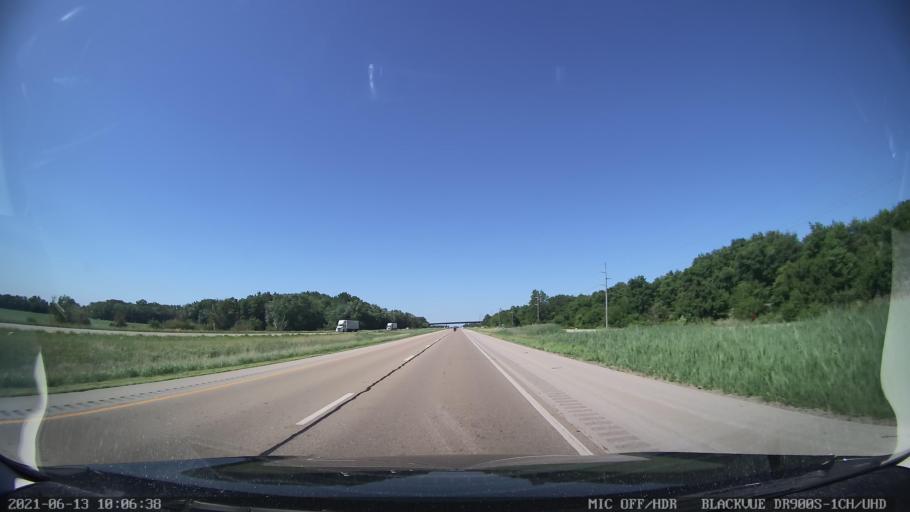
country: US
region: Illinois
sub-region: Logan County
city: Atlanta
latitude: 40.2254
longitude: -89.2727
